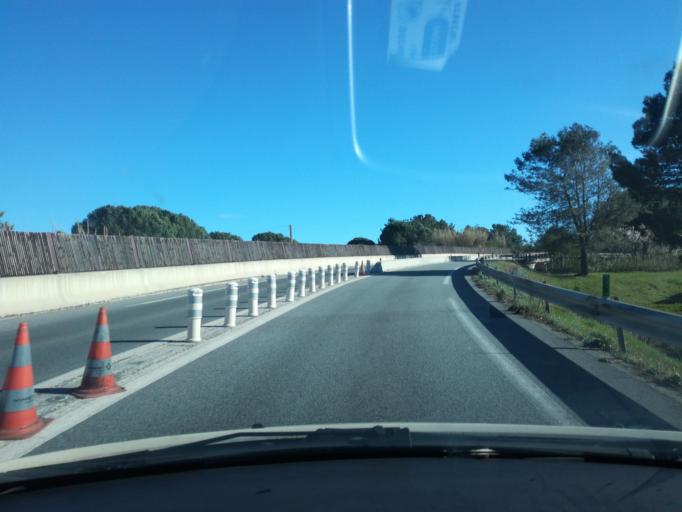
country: FR
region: Provence-Alpes-Cote d'Azur
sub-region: Departement du Var
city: Puget-sur-Argens
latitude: 43.4604
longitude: 6.6885
